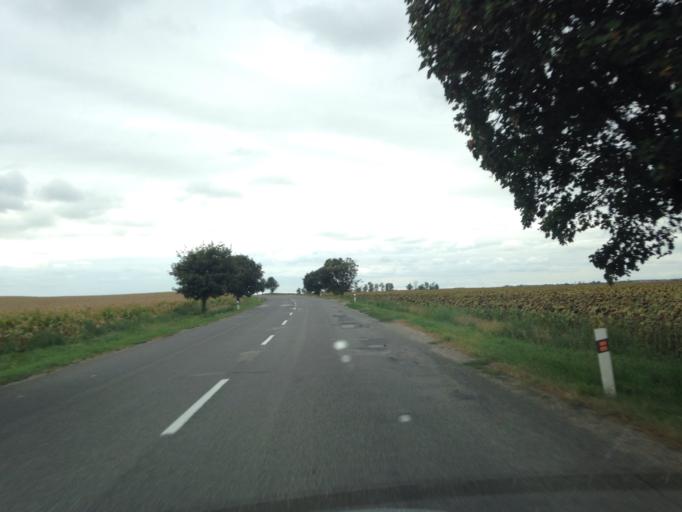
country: SK
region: Nitriansky
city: Svodin
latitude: 47.8922
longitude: 18.3989
